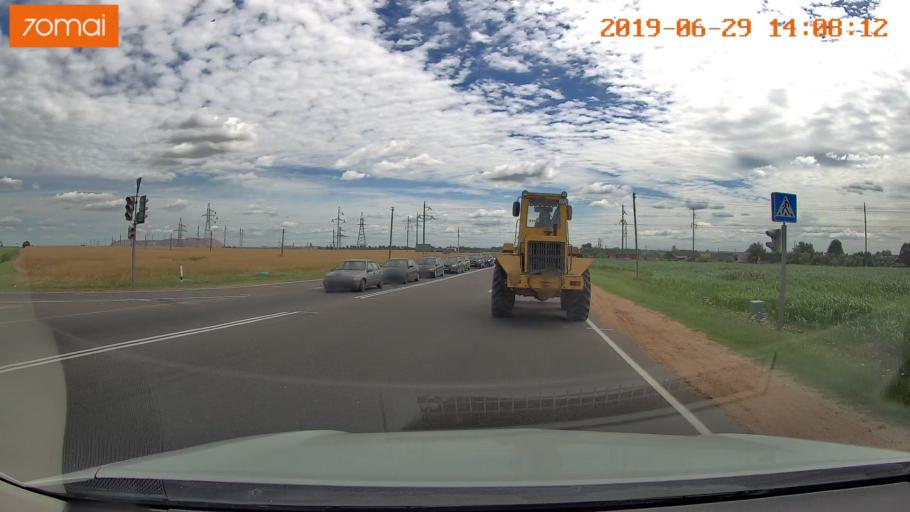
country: BY
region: Minsk
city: Salihorsk
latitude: 52.8526
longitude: 27.4739
